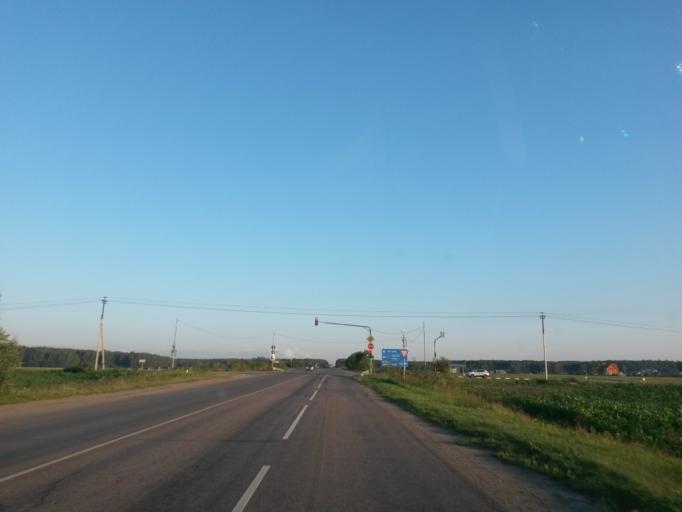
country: RU
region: Moskovskaya
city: Barybino
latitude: 55.1967
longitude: 37.7910
